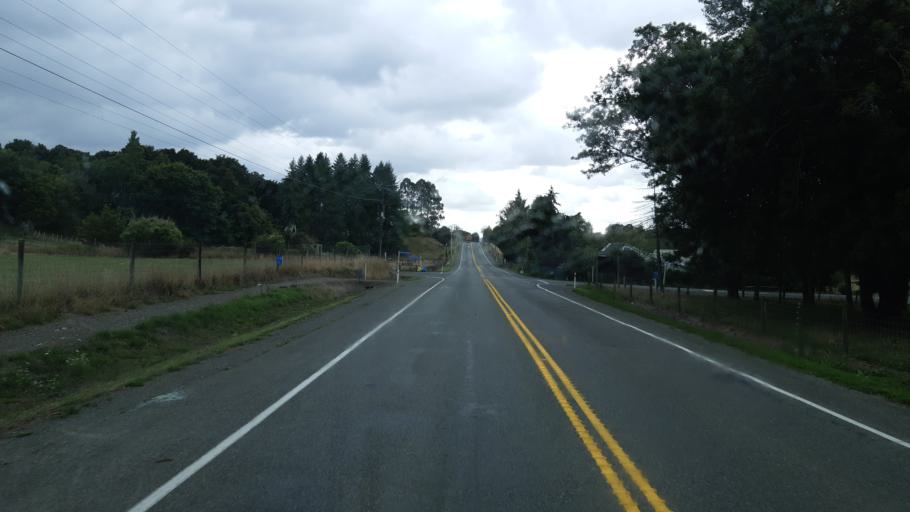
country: NZ
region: Tasman
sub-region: Tasman District
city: Wakefield
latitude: -41.4467
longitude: 172.9630
